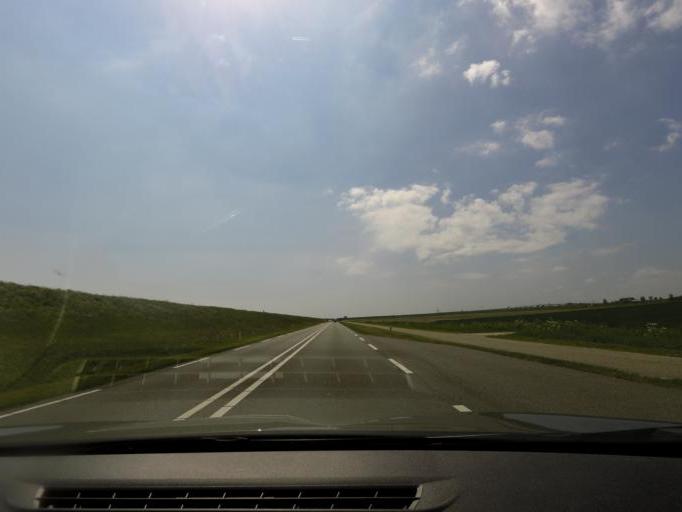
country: NL
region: Zeeland
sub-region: Schouwen-Duiveland
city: Scharendijke
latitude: 51.6354
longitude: 3.9340
